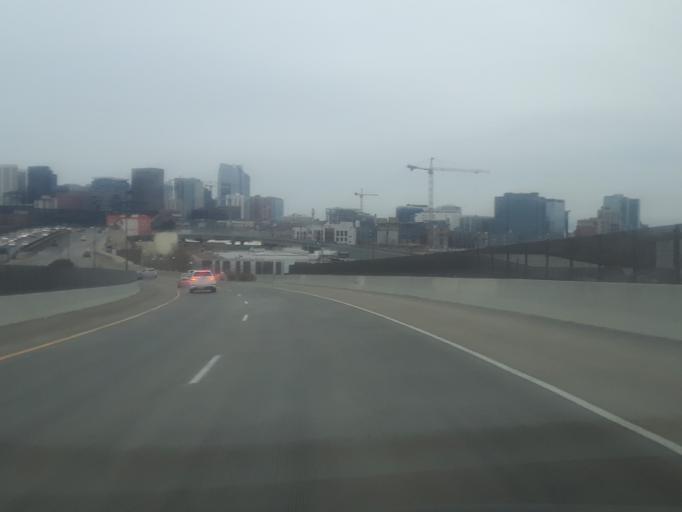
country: US
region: Colorado
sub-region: Denver County
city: Denver
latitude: 39.7664
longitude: -104.9953
